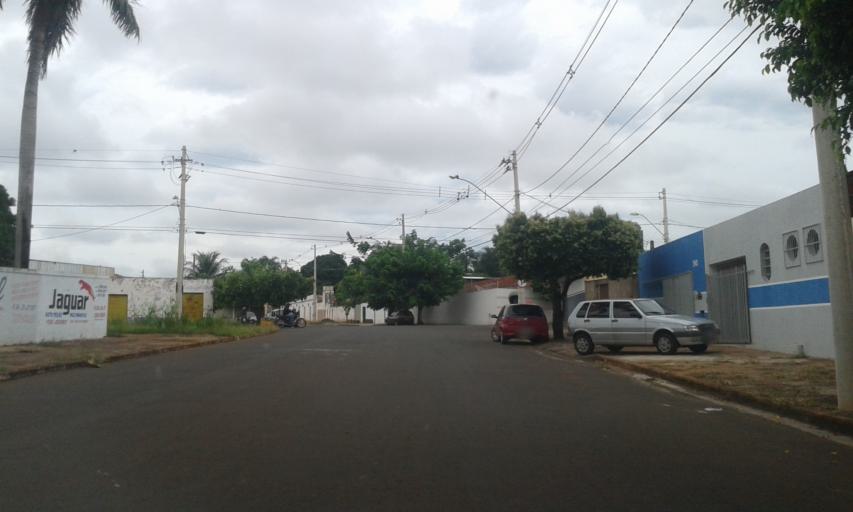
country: BR
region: Minas Gerais
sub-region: Ituiutaba
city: Ituiutaba
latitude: -18.9762
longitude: -49.4513
